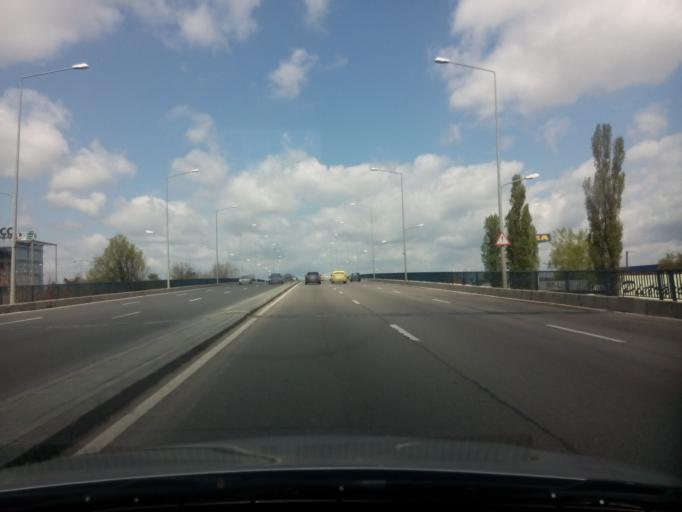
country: RO
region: Ilfov
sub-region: Comuna Otopeni
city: Otopeni
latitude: 44.5026
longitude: 26.0807
